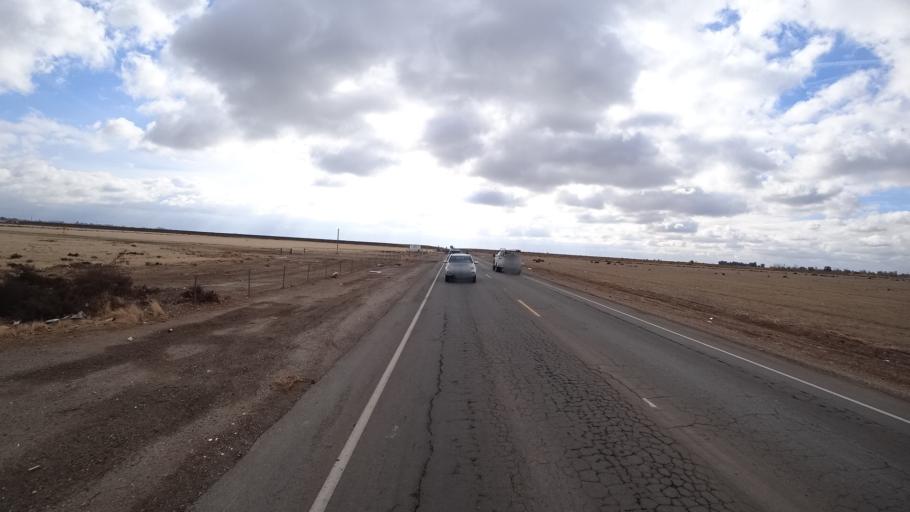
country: US
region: California
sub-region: Kern County
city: Bakersfield
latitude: 35.3435
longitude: -118.9676
